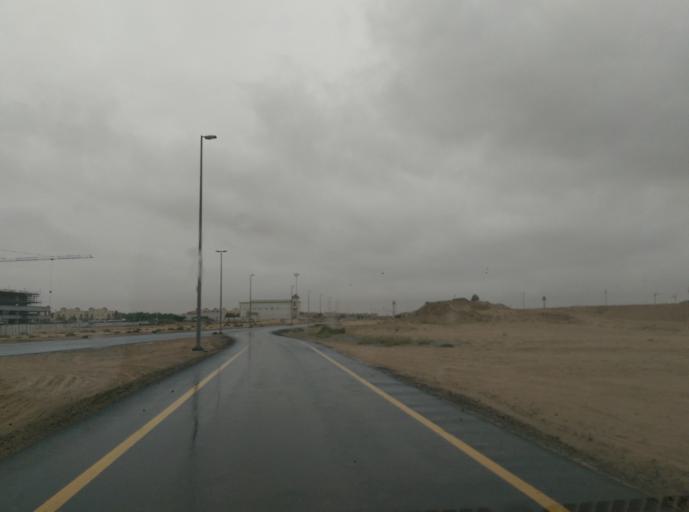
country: AE
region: Dubai
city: Dubai
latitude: 25.0373
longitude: 55.2032
